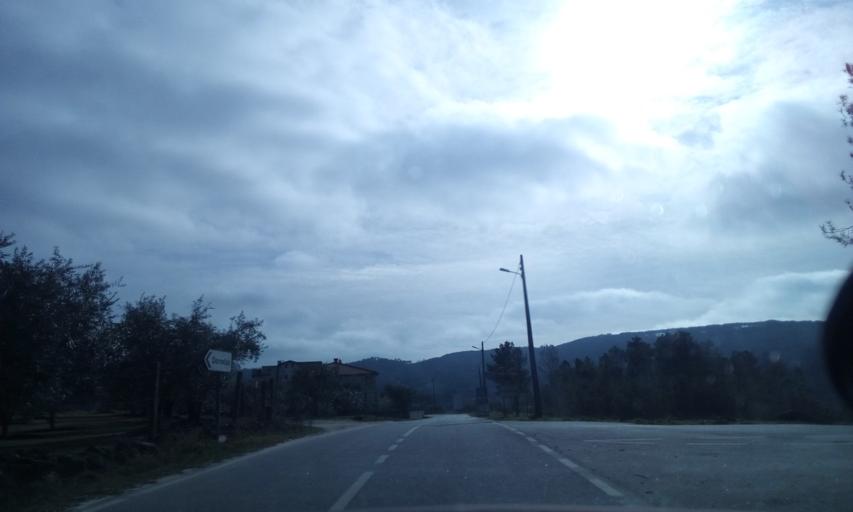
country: PT
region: Guarda
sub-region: Fornos de Algodres
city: Fornos de Algodres
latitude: 40.7042
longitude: -7.5639
